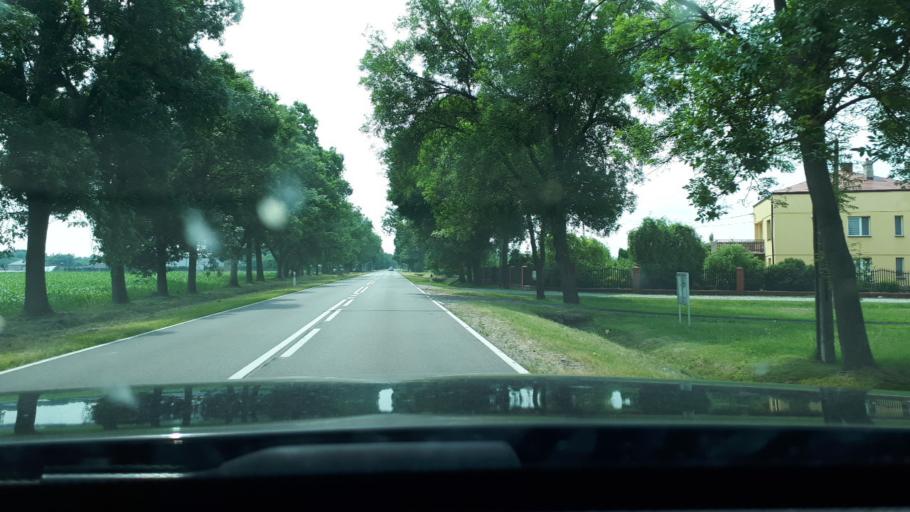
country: PL
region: Masovian Voivodeship
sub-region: Powiat sochaczewski
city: Paprotnia
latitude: 52.2642
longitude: 20.3663
